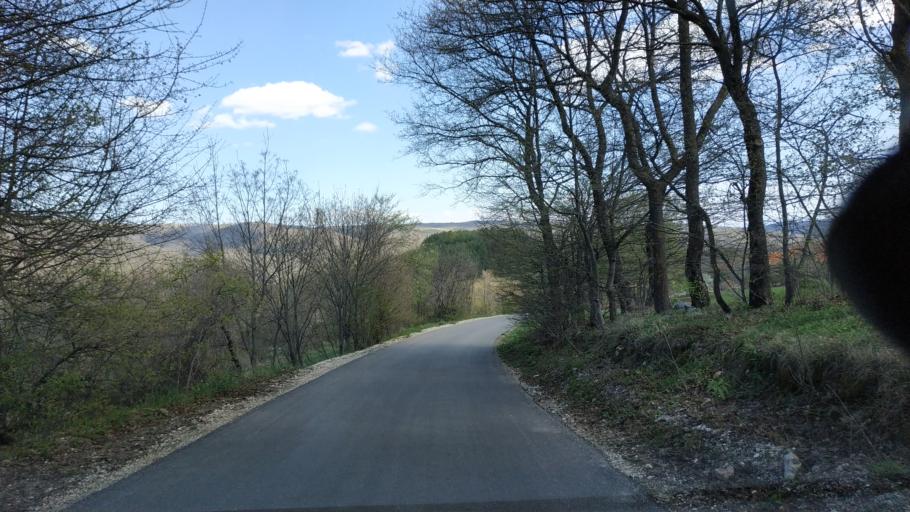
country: RS
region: Central Serbia
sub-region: Zajecarski Okrug
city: Soko Banja
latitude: 43.5754
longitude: 21.8958
